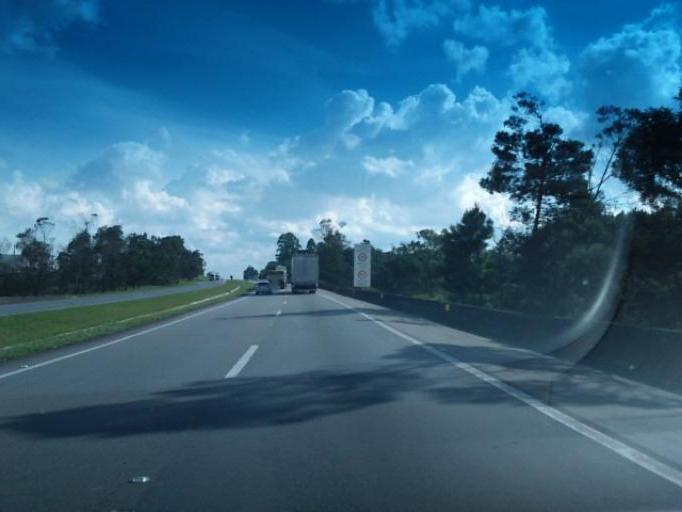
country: BR
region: Parana
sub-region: Quatro Barras
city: Quatro Barras
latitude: -25.3824
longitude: -49.0525
